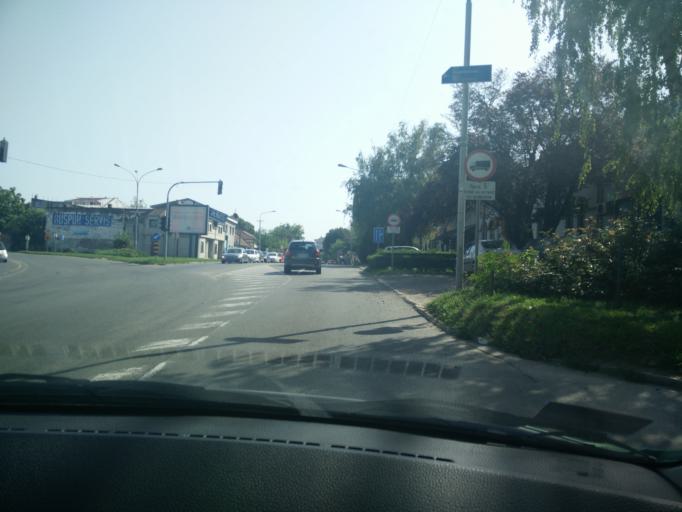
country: RS
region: Autonomna Pokrajina Vojvodina
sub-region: Juznobacki Okrug
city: Novi Sad
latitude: 45.2683
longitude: 19.8427
